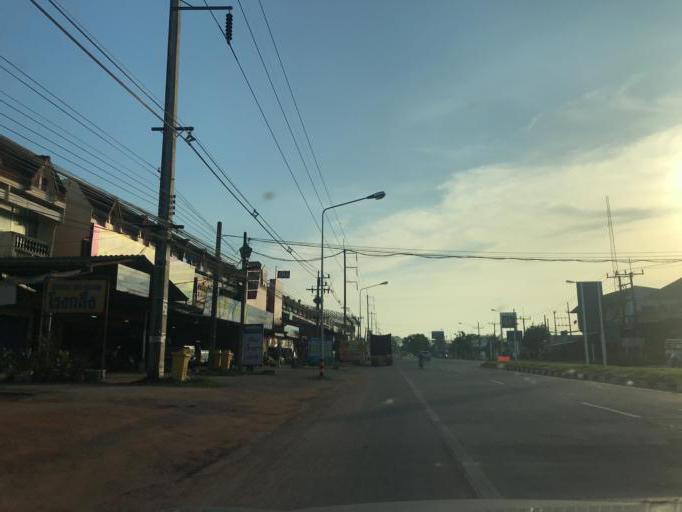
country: TH
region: Phayao
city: Chiang Kham
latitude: 19.5170
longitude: 100.2938
